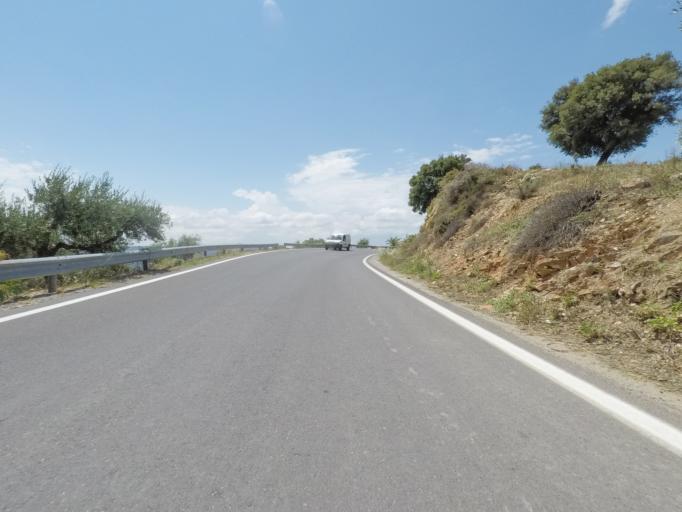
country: GR
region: Crete
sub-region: Nomos Irakleiou
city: Mokhos
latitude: 35.2278
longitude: 25.4605
